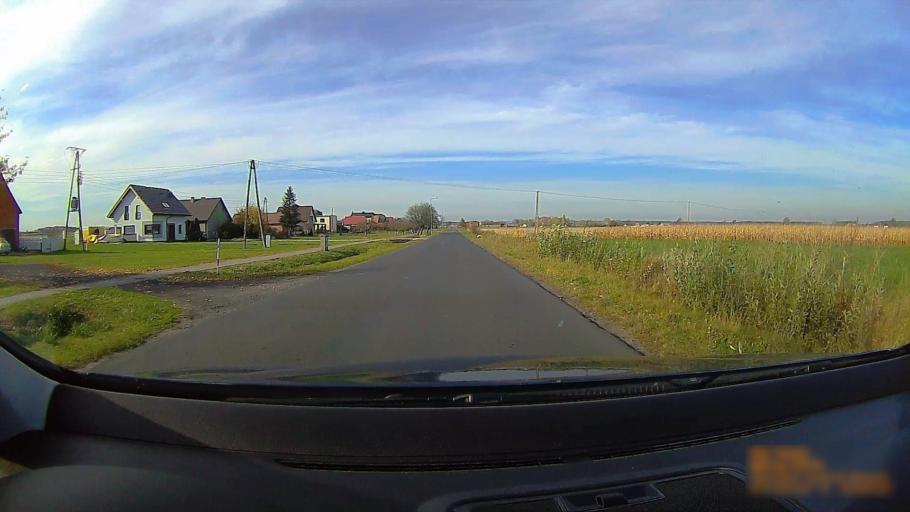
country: PL
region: Greater Poland Voivodeship
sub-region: Powiat ostrzeszowski
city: Doruchow
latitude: 51.4202
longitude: 18.0669
